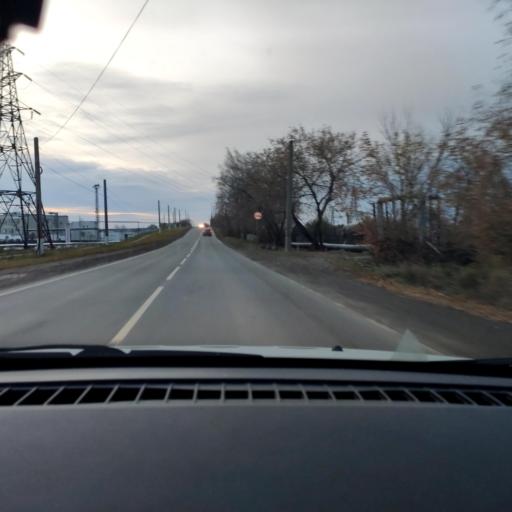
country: RU
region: Perm
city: Gamovo
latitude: 57.9128
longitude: 56.1575
